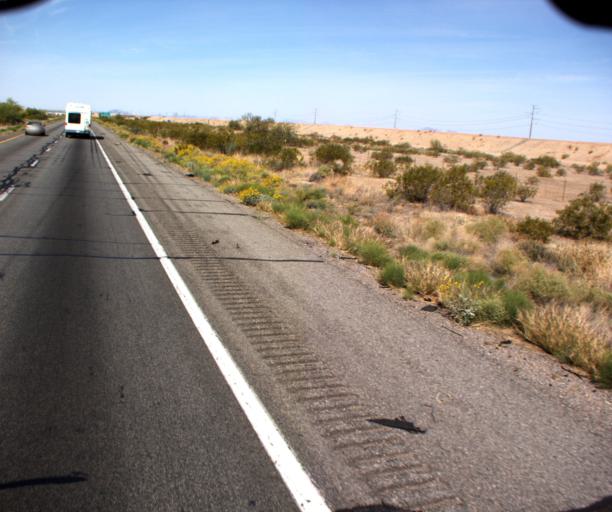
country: US
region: Arizona
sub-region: Maricopa County
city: Buckeye
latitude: 33.4368
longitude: -112.6659
